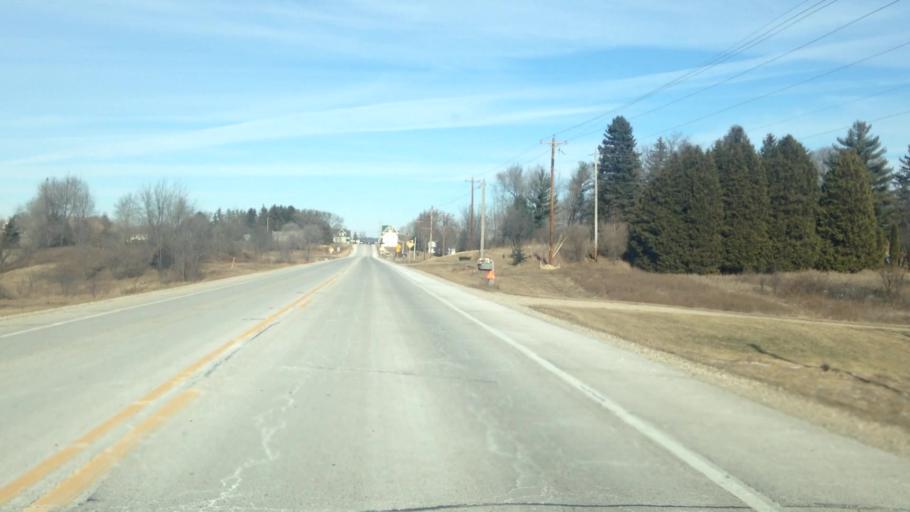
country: US
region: Wisconsin
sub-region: Washington County
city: Richfield
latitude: 43.2614
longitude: -88.2617
